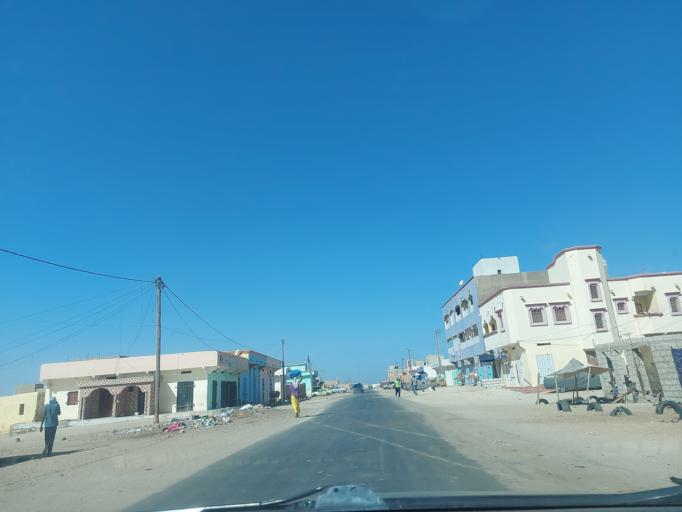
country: MR
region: Nouakchott
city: Nouakchott
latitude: 18.0623
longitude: -16.0039
